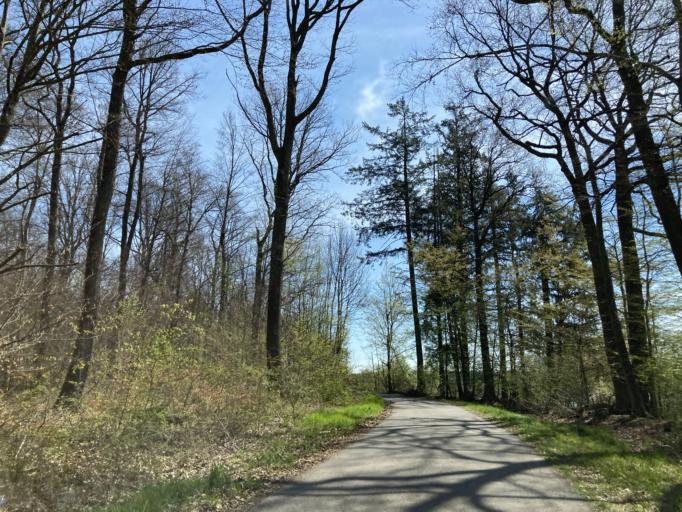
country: DE
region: Baden-Wuerttemberg
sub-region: Tuebingen Region
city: Tuebingen
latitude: 48.5476
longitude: 9.0229
